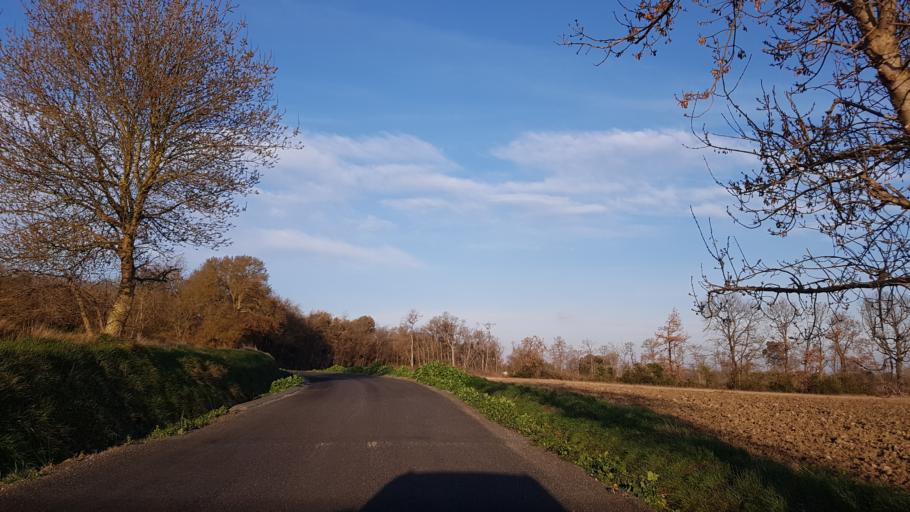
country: FR
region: Languedoc-Roussillon
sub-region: Departement de l'Aude
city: Villeneuve-la-Comptal
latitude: 43.2829
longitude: 1.9359
